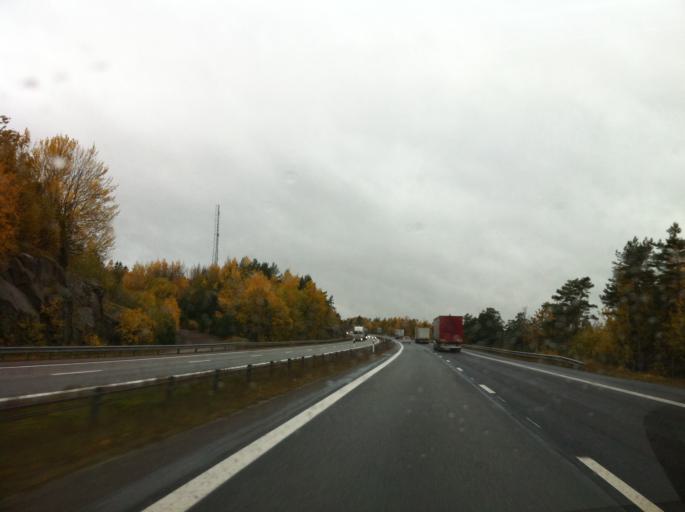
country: SE
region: Joenkoeping
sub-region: Jonkopings Kommun
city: Kaxholmen
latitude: 57.9612
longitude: 14.3551
